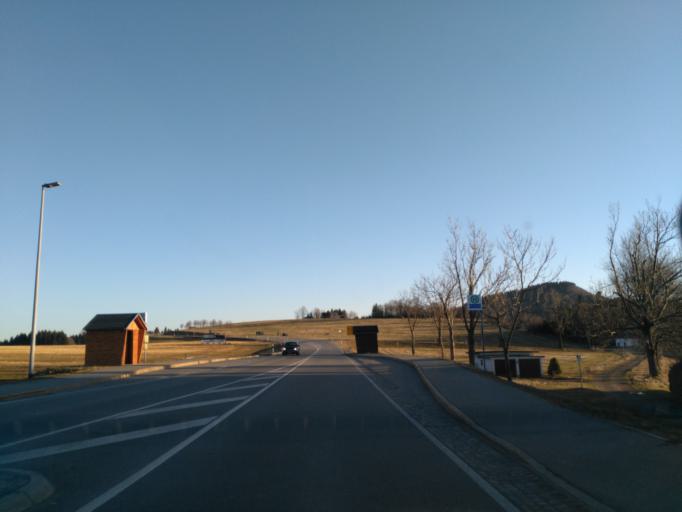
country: DE
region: Saxony
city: Barenstein
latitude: 50.5226
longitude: 13.0310
